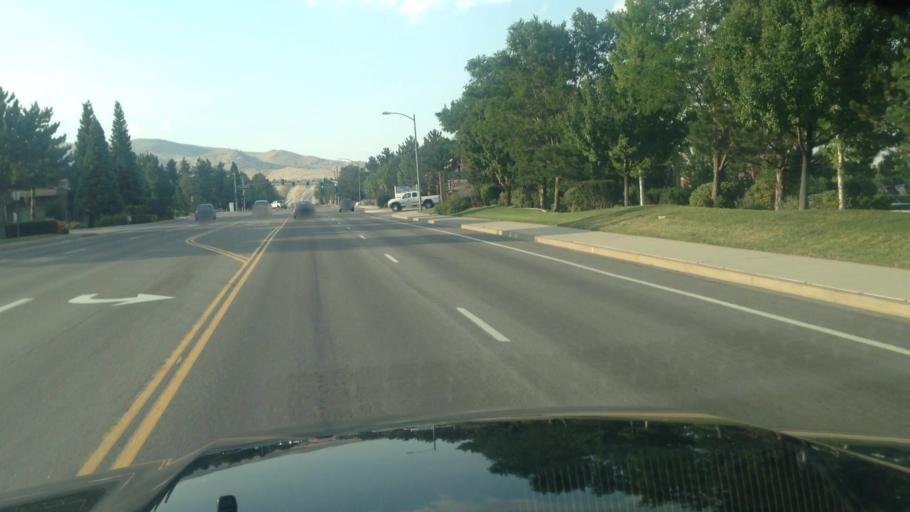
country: US
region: Nevada
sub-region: Washoe County
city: Mogul
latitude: 39.5274
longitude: -119.8821
